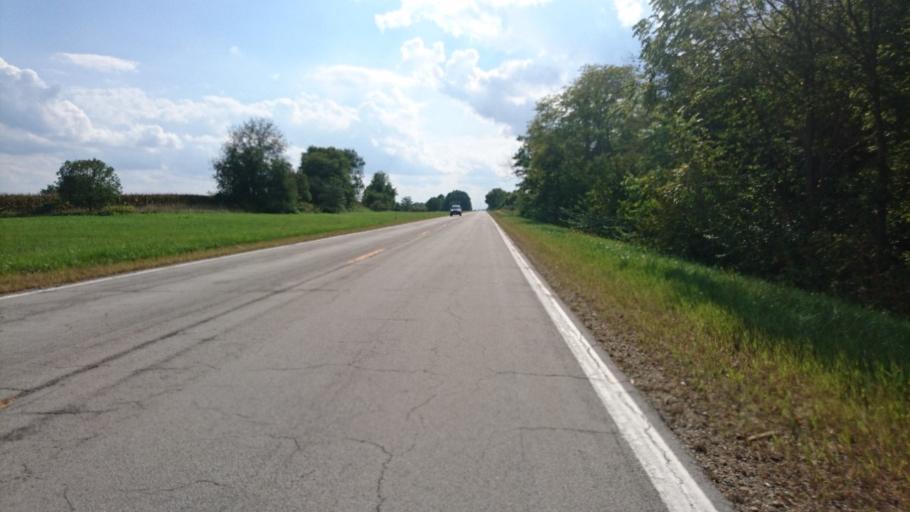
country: US
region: Illinois
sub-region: Logan County
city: Atlanta
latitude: 40.3489
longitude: -89.1291
